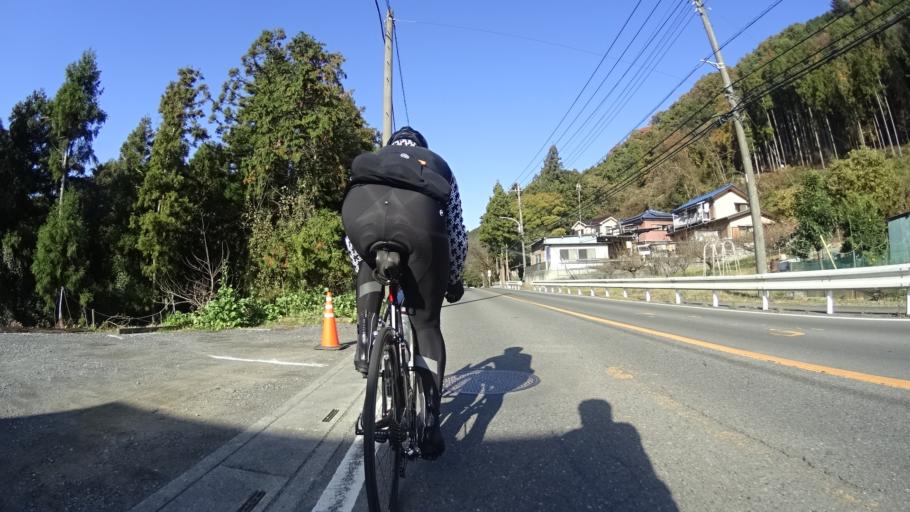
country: JP
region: Saitama
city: Hanno
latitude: 35.8663
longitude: 139.2848
